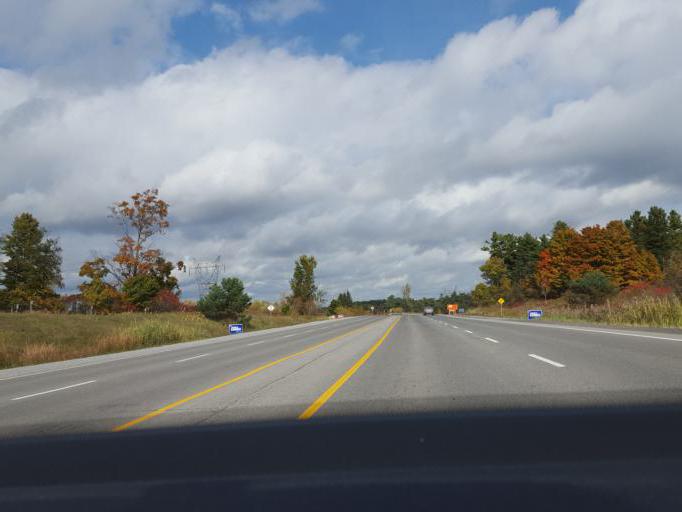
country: CA
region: Ontario
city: Pickering
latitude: 43.8837
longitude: -79.0972
